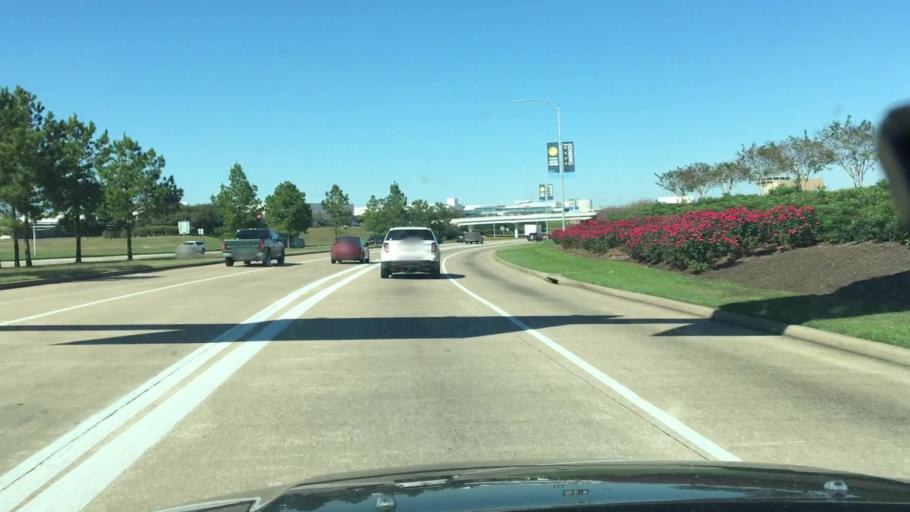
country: US
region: Texas
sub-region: Harris County
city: Aldine
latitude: 29.9759
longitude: -95.3422
